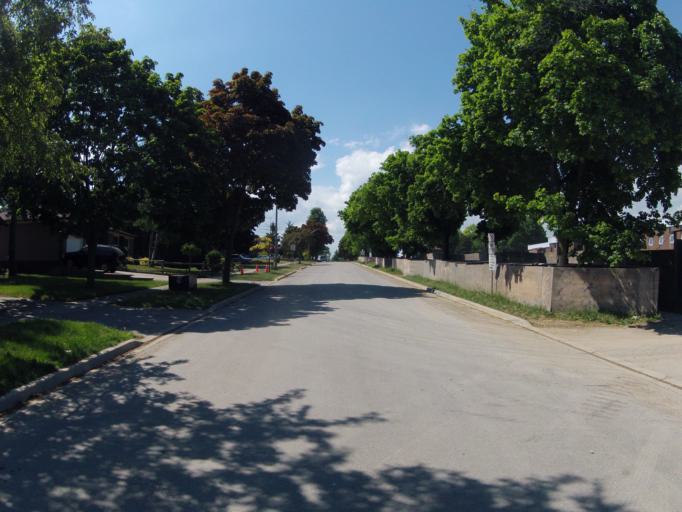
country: CA
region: Ontario
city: Oakville
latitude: 43.5081
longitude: -79.6465
